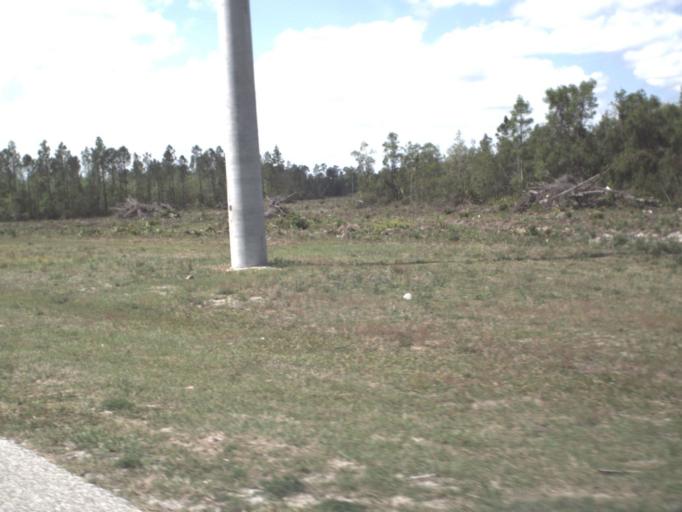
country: US
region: Florida
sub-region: Flagler County
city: Bunnell
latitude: 29.5211
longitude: -81.2628
